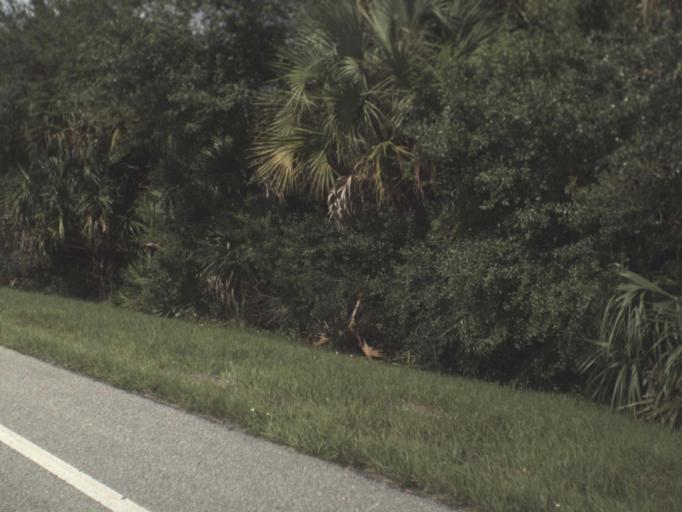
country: US
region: Florida
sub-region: Sarasota County
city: Plantation
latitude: 27.0807
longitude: -82.3315
